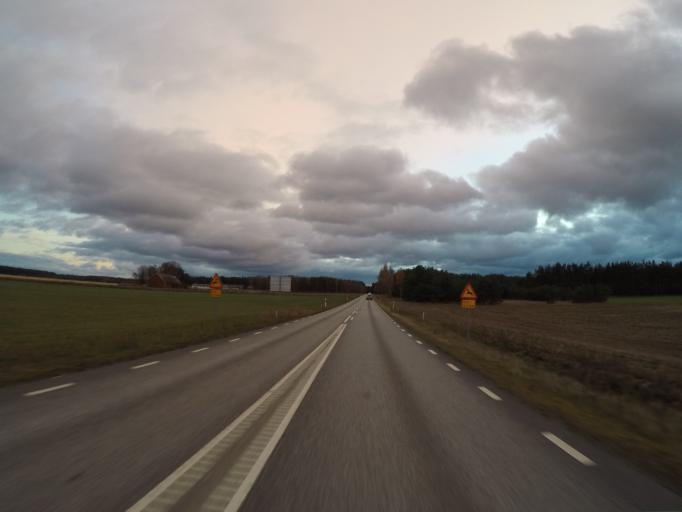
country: SE
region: Skane
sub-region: Kristianstads Kommun
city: Degeberga
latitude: 55.9229
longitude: 14.0738
